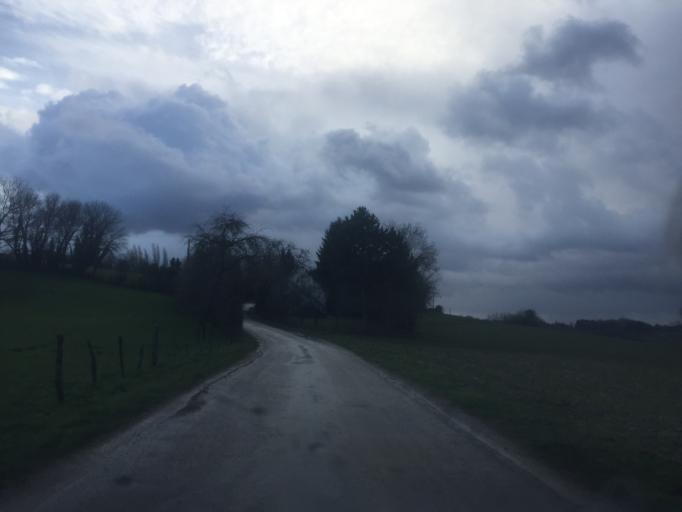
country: FR
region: Franche-Comte
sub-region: Departement du Jura
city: Fraisans
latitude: 47.1755
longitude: 5.7712
